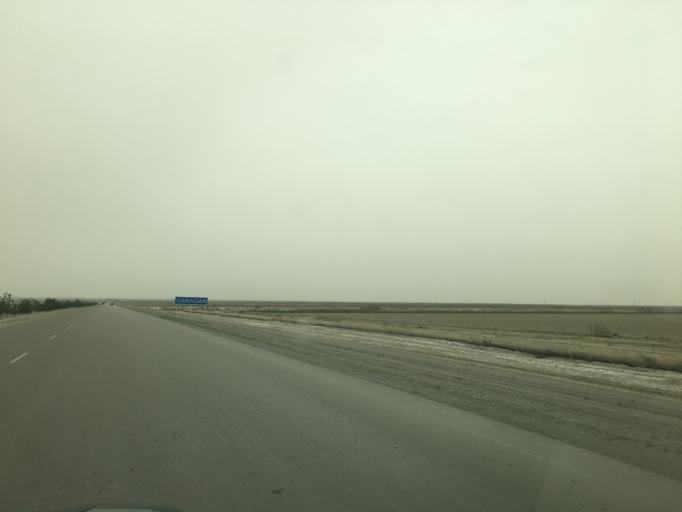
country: TM
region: Ahal
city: Baharly
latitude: 38.3725
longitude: 57.5145
